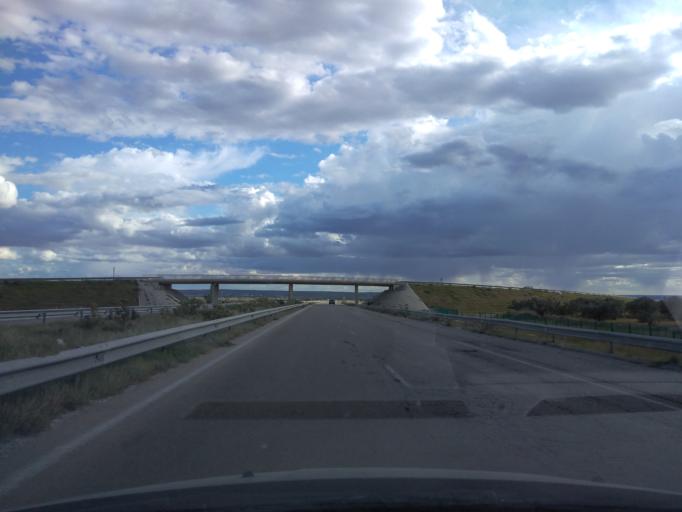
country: TN
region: Al Munastir
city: Manzil Kamil
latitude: 35.5214
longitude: 10.6264
